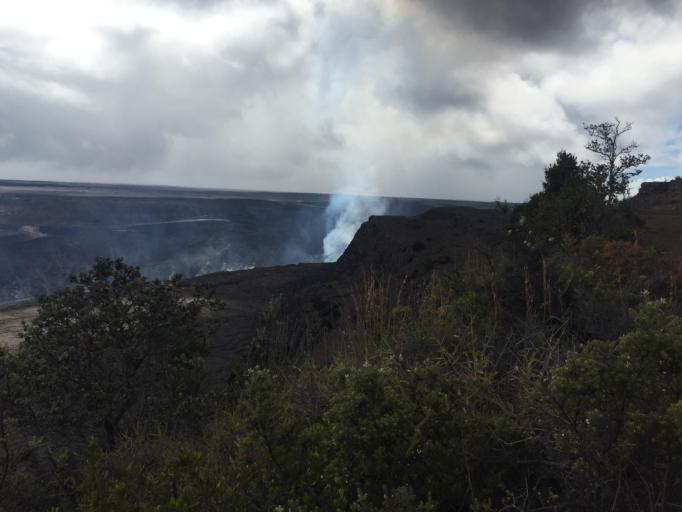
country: US
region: Hawaii
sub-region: Hawaii County
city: Volcano
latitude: 19.4231
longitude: -155.2841
